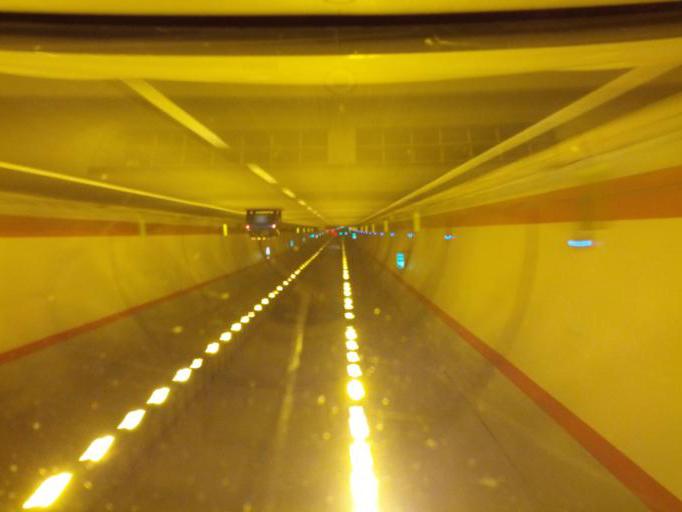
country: IT
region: Friuli Venezia Giulia
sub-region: Provincia di Trieste
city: Domio
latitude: 45.6042
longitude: 13.8233
